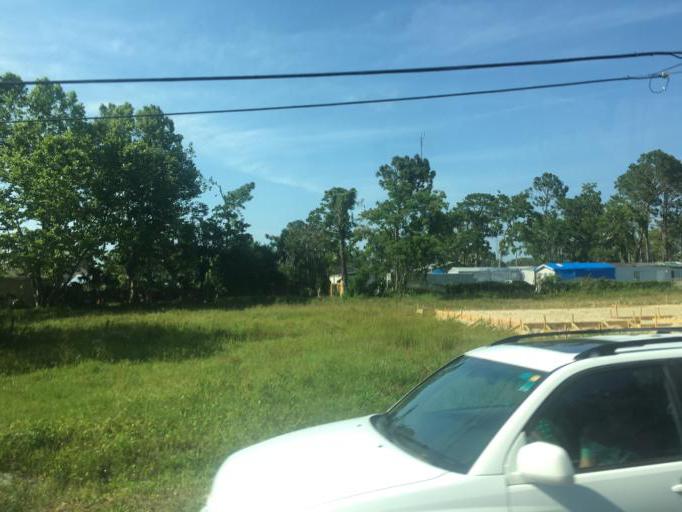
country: US
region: Florida
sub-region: Bay County
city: Panama City Beach
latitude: 30.1749
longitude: -85.7833
